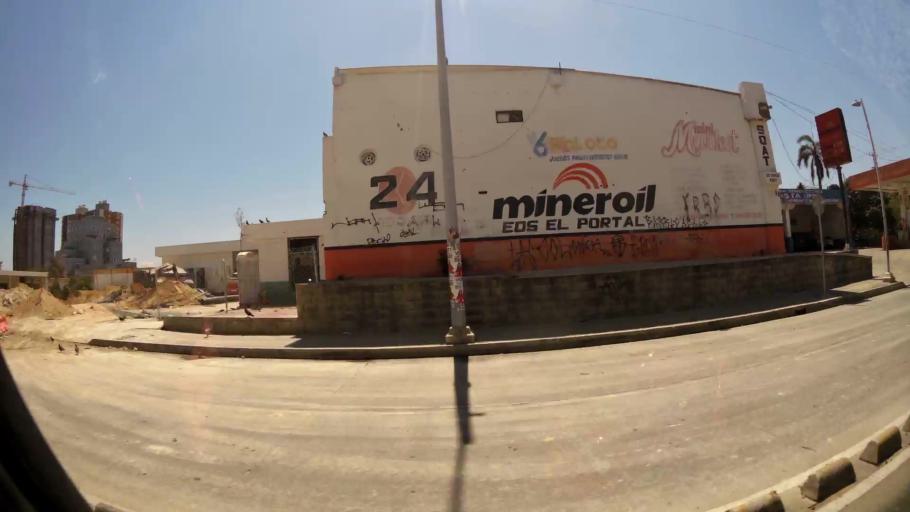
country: CO
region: Atlantico
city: Barranquilla
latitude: 10.9880
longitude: -74.7874
